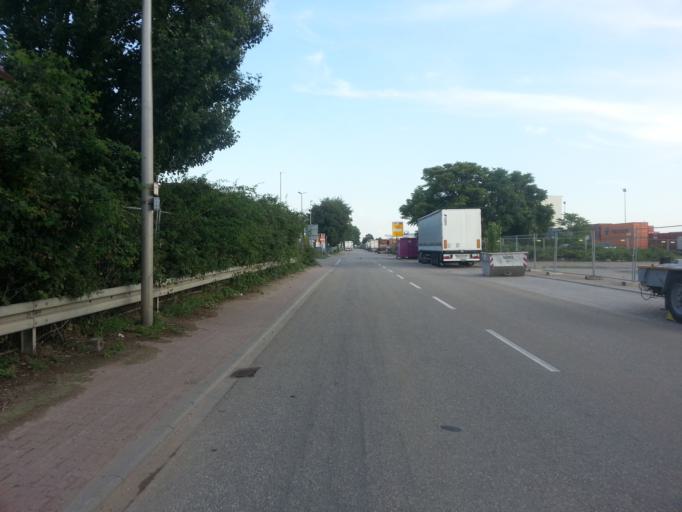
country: DE
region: Rheinland-Pfalz
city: Ludwigshafen am Rhein
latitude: 49.5055
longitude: 8.4436
